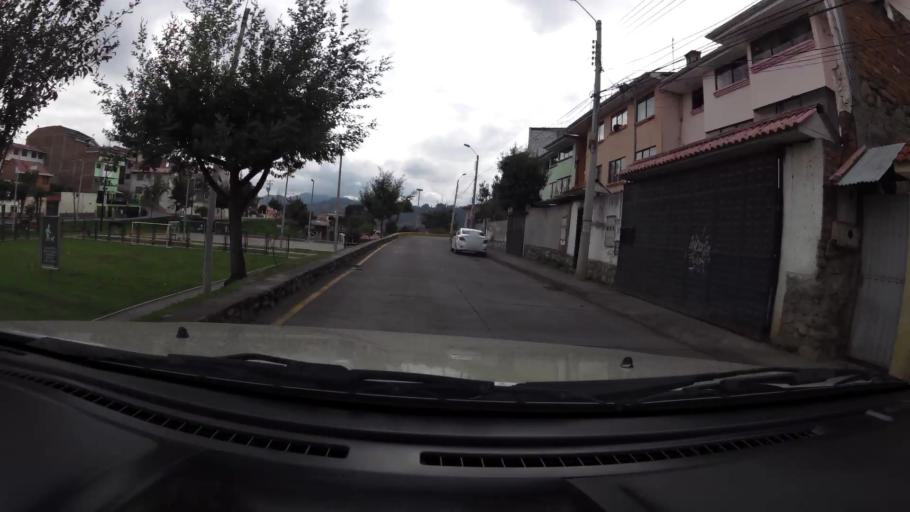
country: EC
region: Azuay
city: Cuenca
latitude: -2.8994
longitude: -78.9875
